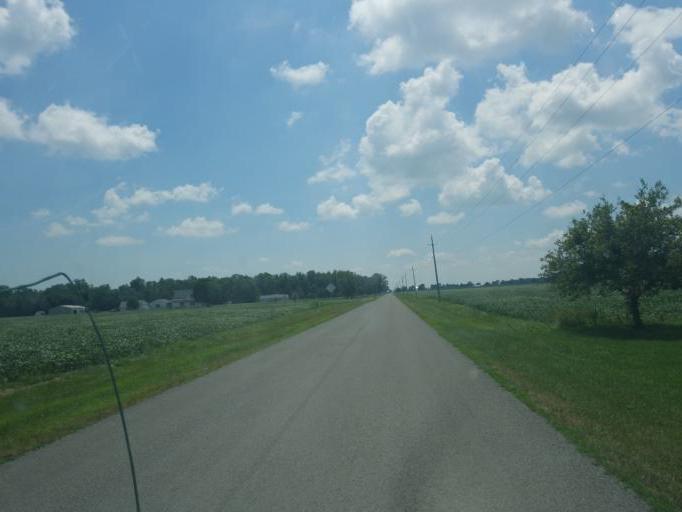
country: US
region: Ohio
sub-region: Mercer County
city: Celina
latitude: 40.5952
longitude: -84.4940
